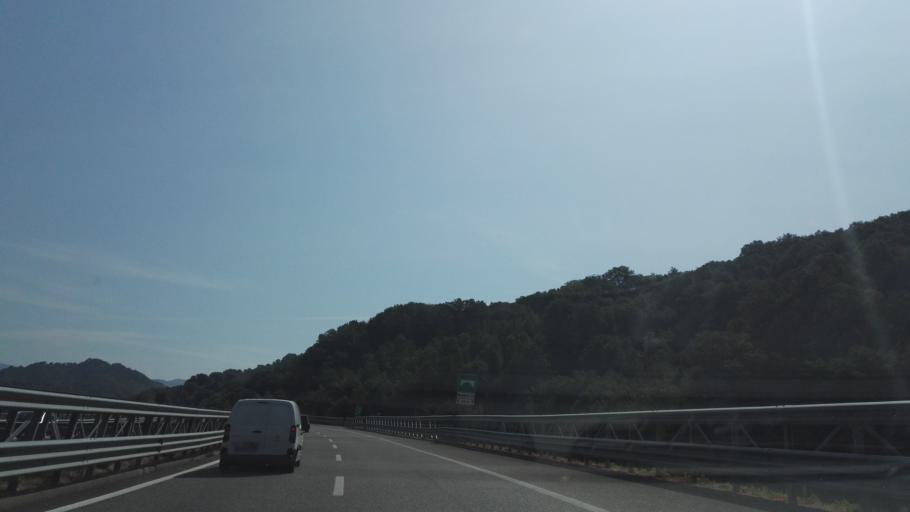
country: IT
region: Calabria
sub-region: Provincia di Catanzaro
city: San Mango d'Aquino
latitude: 39.0799
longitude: 16.2052
